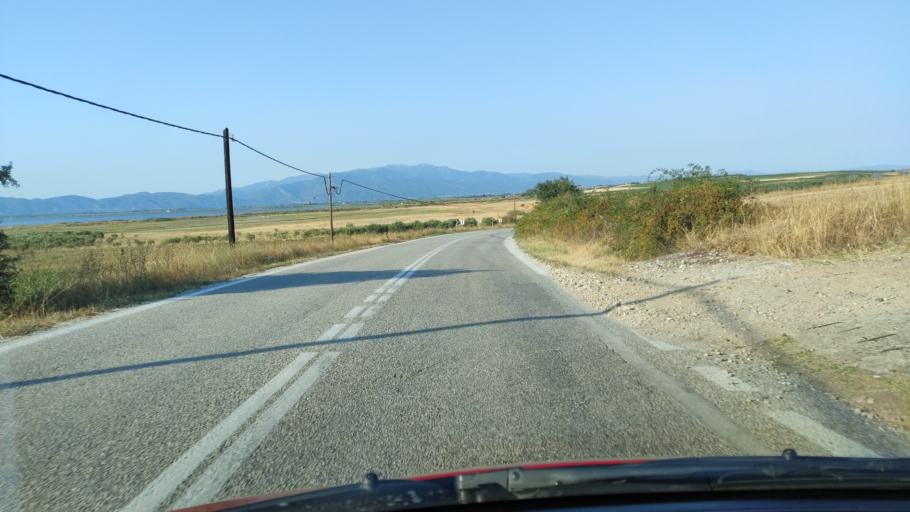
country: GR
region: East Macedonia and Thrace
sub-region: Nomos Rodopis
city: Iasmos
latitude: 40.9949
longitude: 25.1671
